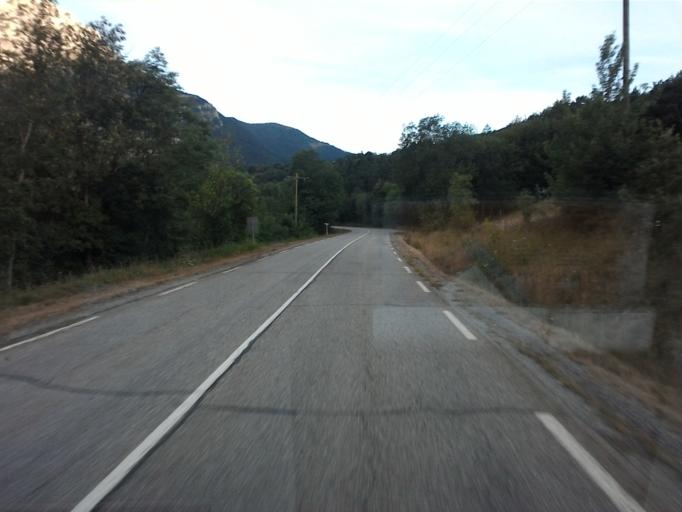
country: FR
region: Provence-Alpes-Cote d'Azur
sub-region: Departement des Hautes-Alpes
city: Saint-Bonnet-en-Champsaur
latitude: 44.7780
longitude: 6.0051
